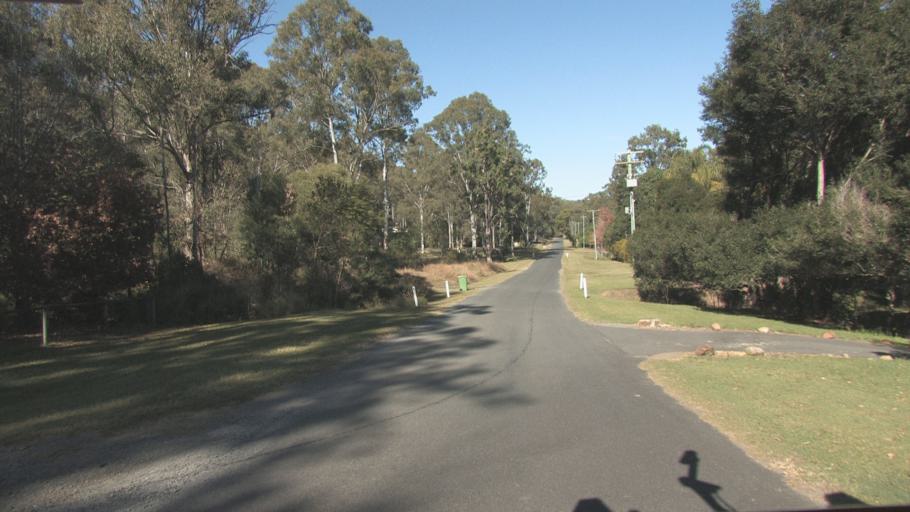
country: AU
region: Queensland
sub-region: Logan
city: Windaroo
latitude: -27.7803
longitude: 153.1481
